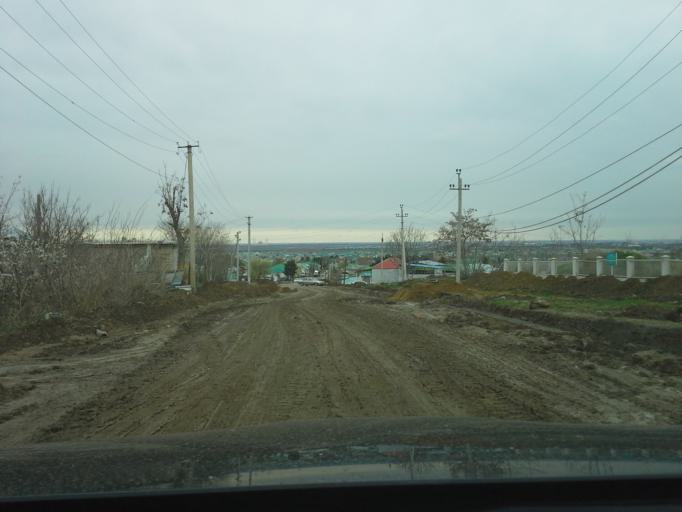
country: TM
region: Ahal
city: Abadan
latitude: 37.9612
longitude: 58.2110
